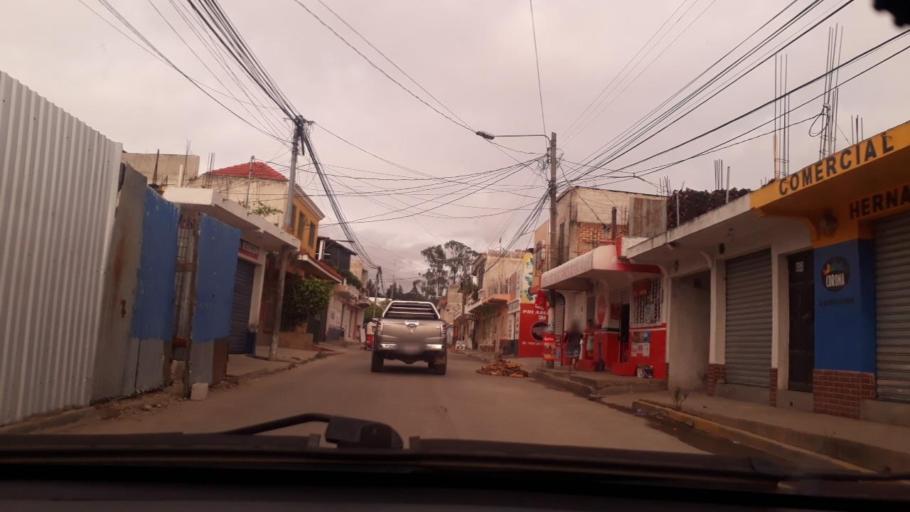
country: GT
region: Jalapa
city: Jalapa
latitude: 14.6407
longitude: -89.9897
